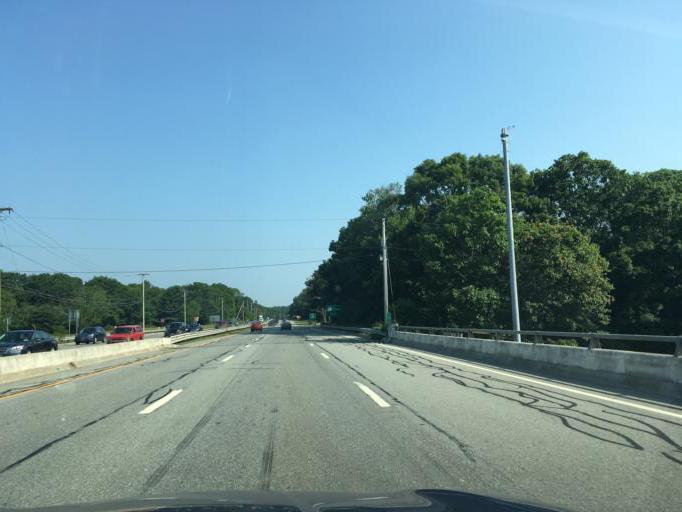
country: US
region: Rhode Island
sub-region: Washington County
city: North Kingstown
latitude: 41.5300
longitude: -71.4660
